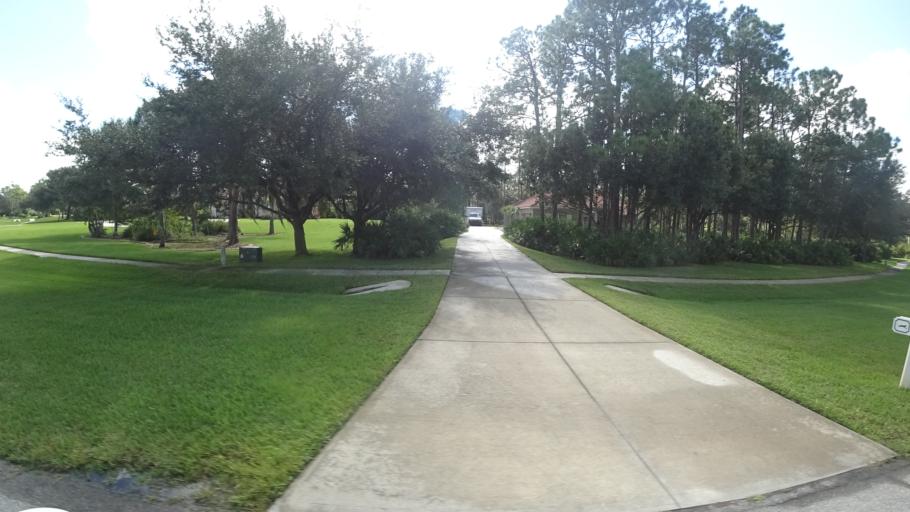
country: US
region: Florida
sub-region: Sarasota County
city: The Meadows
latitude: 27.4005
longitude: -82.3189
